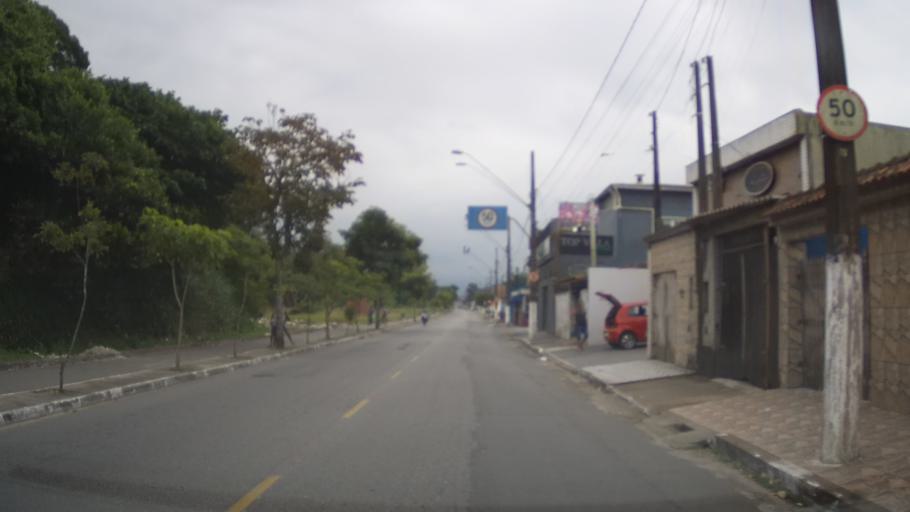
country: BR
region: Sao Paulo
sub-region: Praia Grande
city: Praia Grande
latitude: -24.0074
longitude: -46.4507
